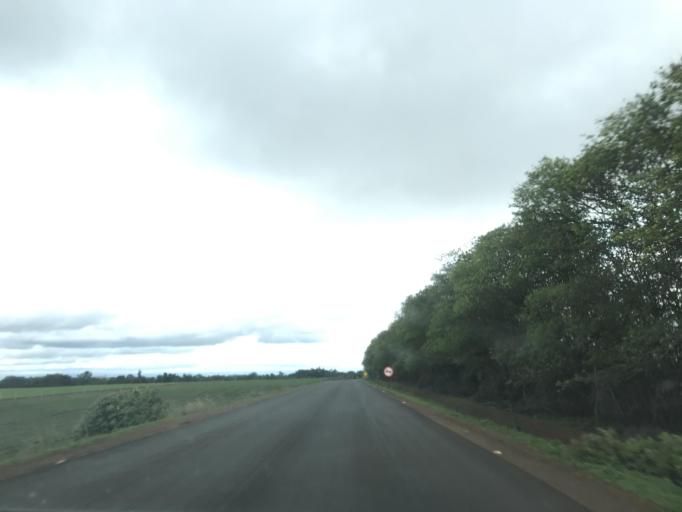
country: BR
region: Goias
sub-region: Vianopolis
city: Vianopolis
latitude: -16.7908
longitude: -48.5214
